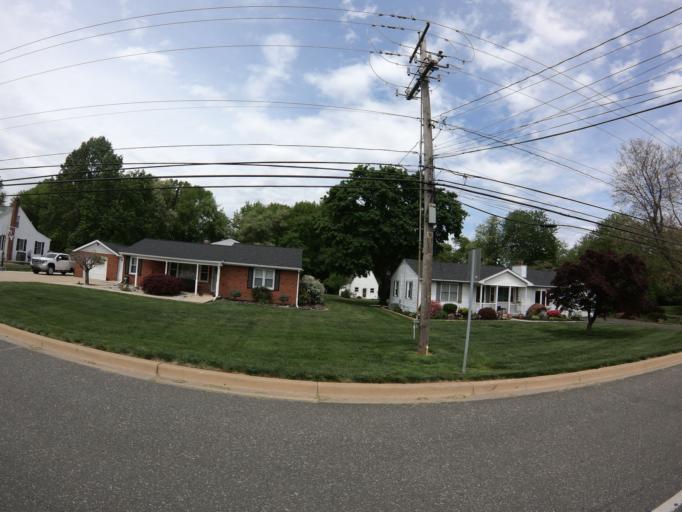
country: US
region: Delaware
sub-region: New Castle County
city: Newport
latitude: 39.6873
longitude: -75.6390
